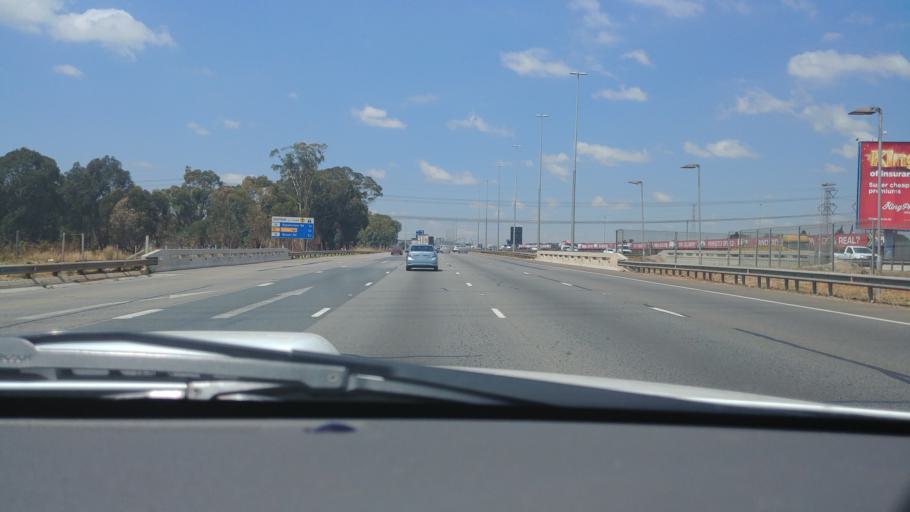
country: ZA
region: Gauteng
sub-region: Ekurhuleni Metropolitan Municipality
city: Tembisa
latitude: -26.0109
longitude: 28.2556
